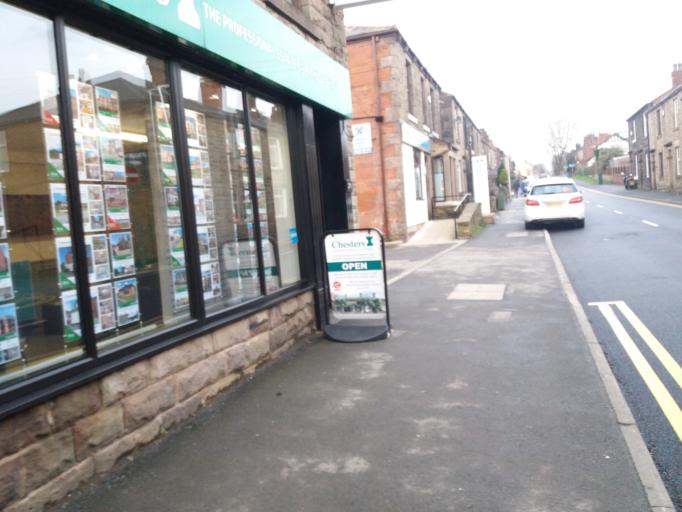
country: GB
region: England
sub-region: Lancashire
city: Adlington
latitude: 53.6178
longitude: -2.5970
